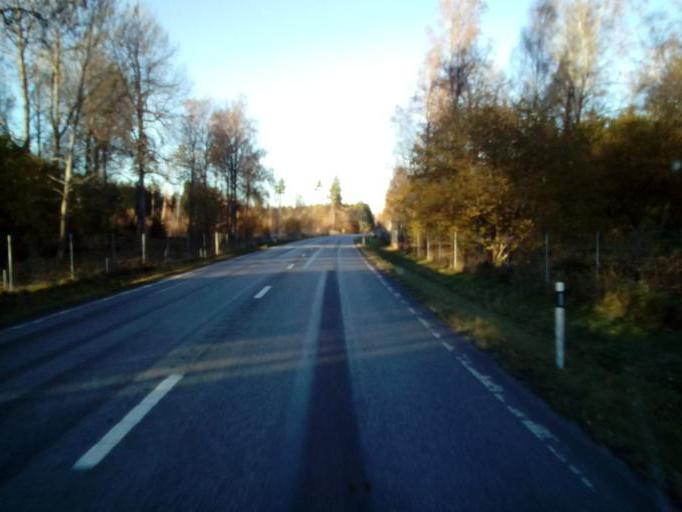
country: SE
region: OErebro
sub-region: Hallsbergs Kommun
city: Palsboda
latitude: 58.9735
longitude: 15.4085
